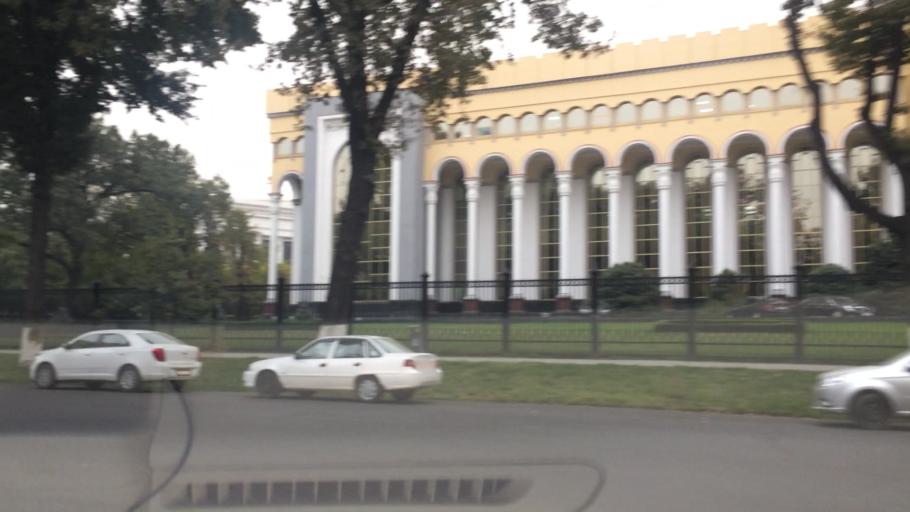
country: UZ
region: Toshkent Shahri
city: Tashkent
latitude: 41.3083
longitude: 69.2792
